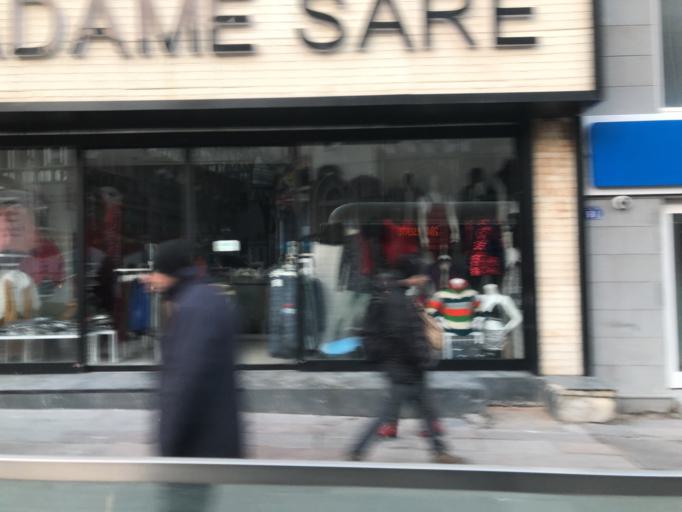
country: TR
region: Ankara
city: Ankara
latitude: 39.9428
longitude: 32.8544
